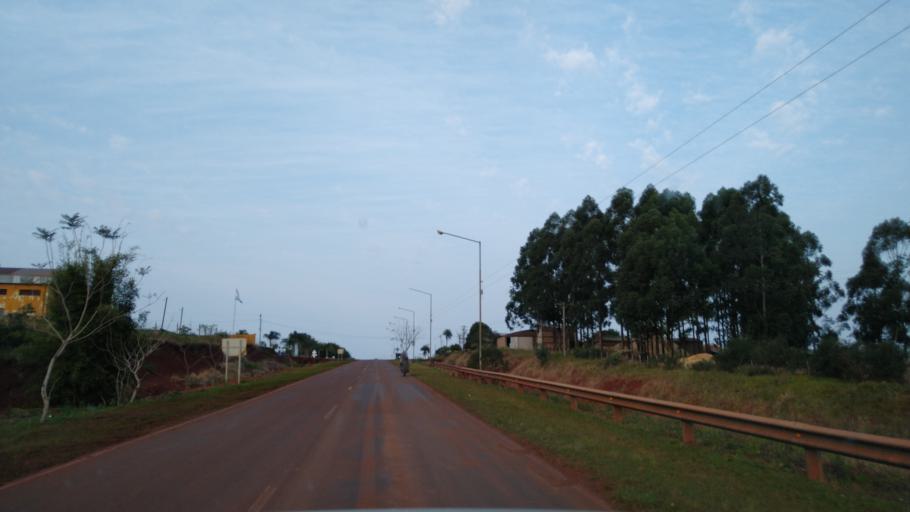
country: AR
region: Corrientes
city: San Carlos
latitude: -27.7518
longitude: -55.8896
